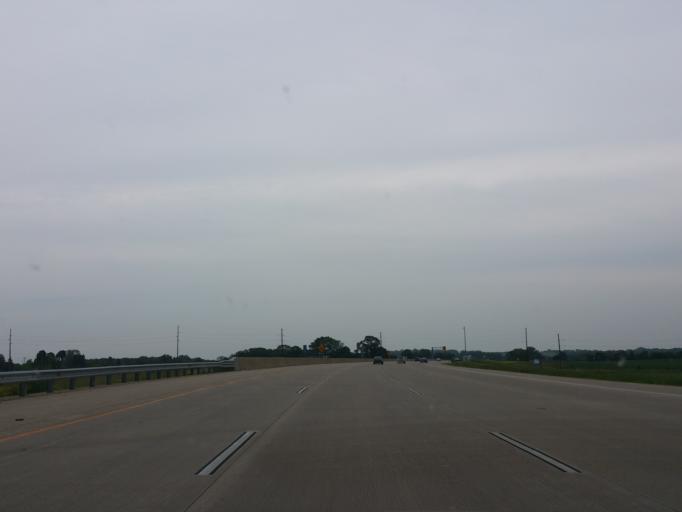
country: US
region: Wisconsin
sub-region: Dane County
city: Monona
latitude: 43.1032
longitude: -89.2715
